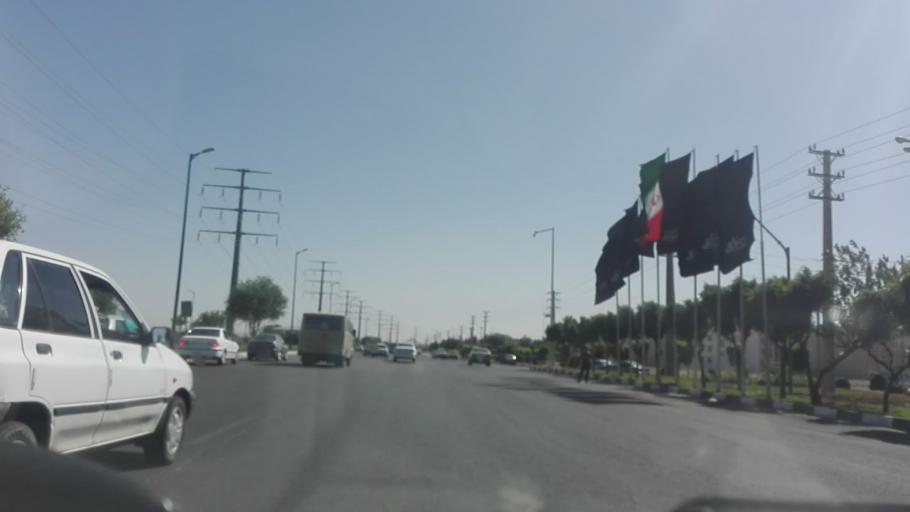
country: IR
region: Tehran
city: Shahre Jadide Andisheh
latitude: 35.6687
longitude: 51.0228
